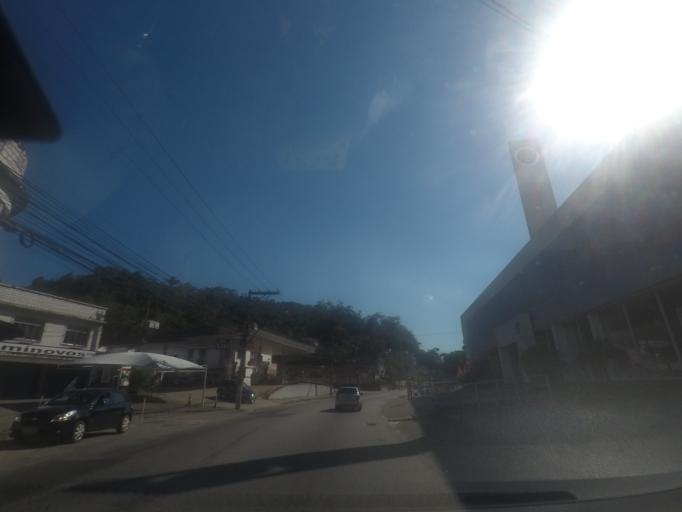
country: BR
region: Rio de Janeiro
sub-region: Petropolis
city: Petropolis
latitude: -22.5289
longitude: -43.1962
